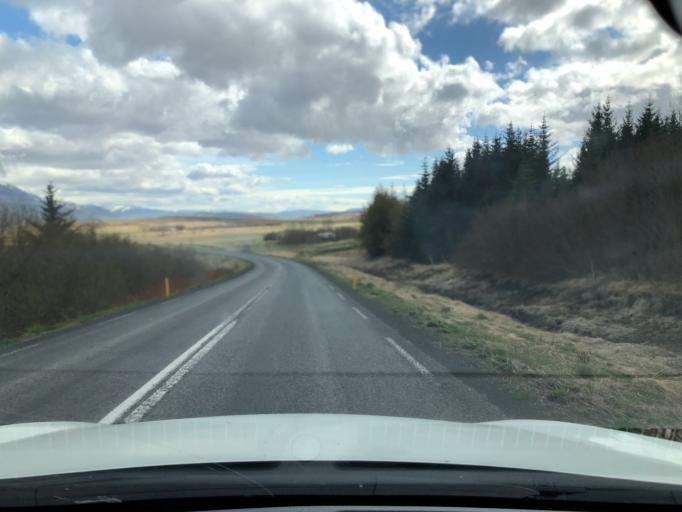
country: IS
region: Northwest
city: Saudarkrokur
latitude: 65.5466
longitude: -19.4750
